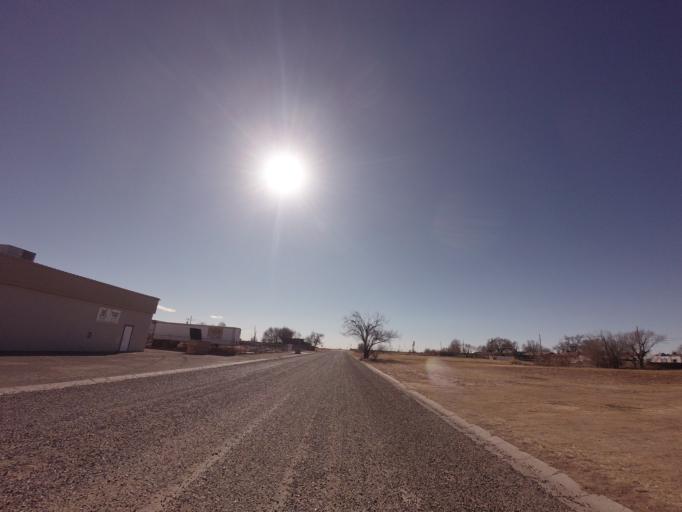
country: US
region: New Mexico
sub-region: Curry County
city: Clovis
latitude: 34.4032
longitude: -103.2399
